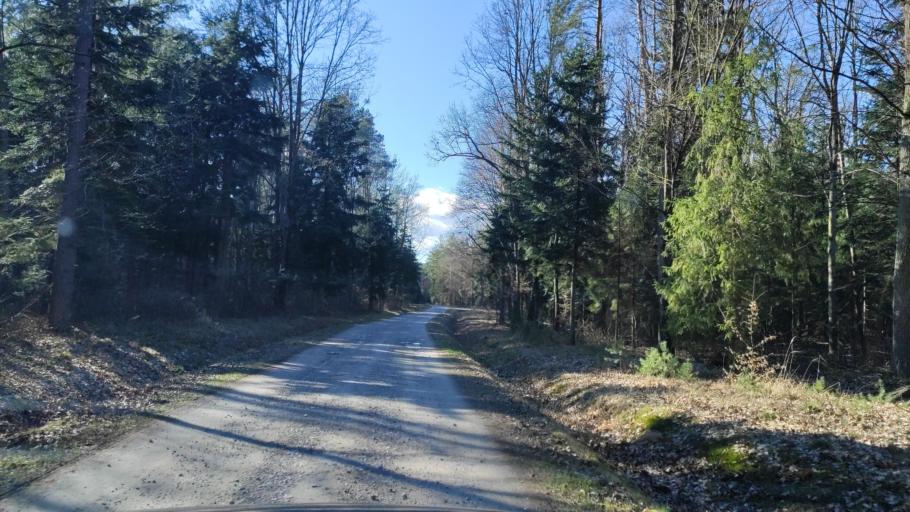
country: PL
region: Masovian Voivodeship
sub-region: Powiat radomski
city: Jastrzebia
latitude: 51.4744
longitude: 21.2723
